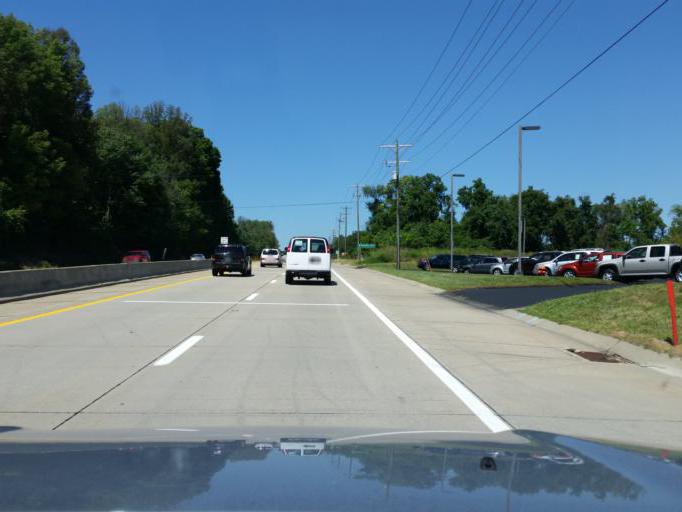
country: US
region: Pennsylvania
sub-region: Westmoreland County
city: Delmont
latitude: 40.4096
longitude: -79.6168
